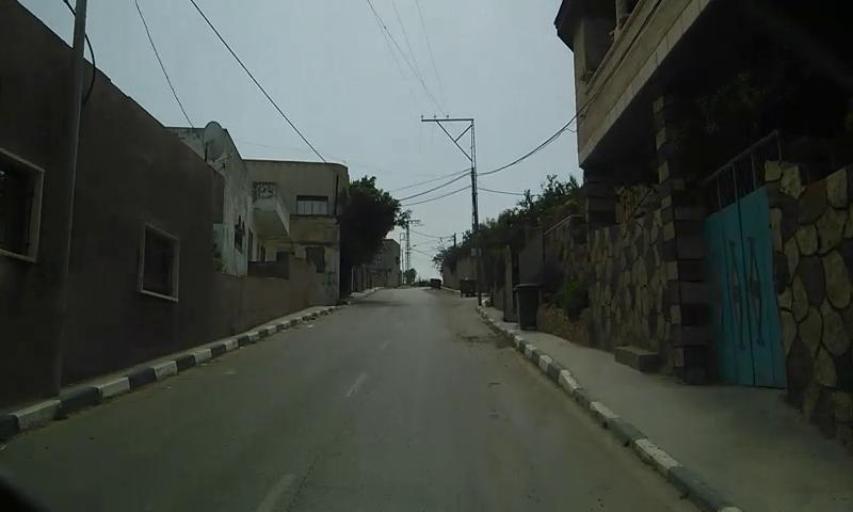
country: PS
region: West Bank
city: Silat al Harithiyah
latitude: 32.5226
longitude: 35.2229
